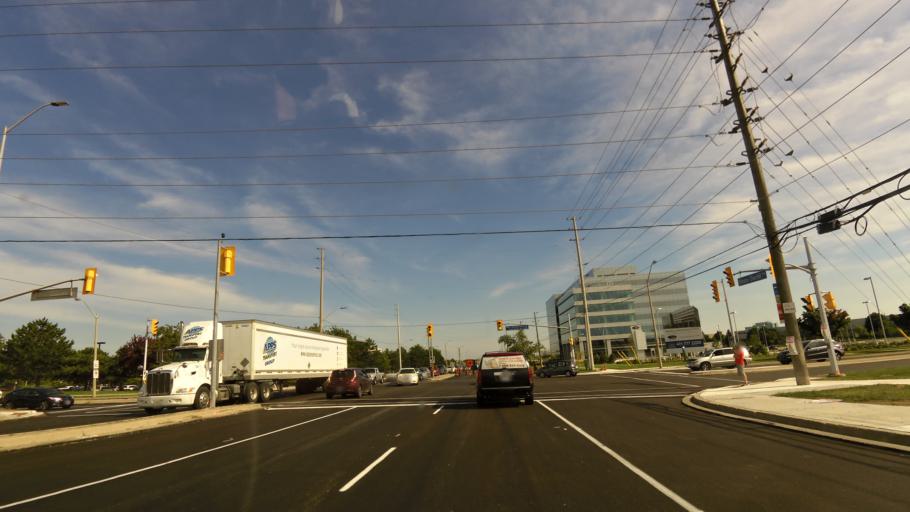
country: CA
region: Ontario
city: Mississauga
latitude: 43.5161
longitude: -79.6726
